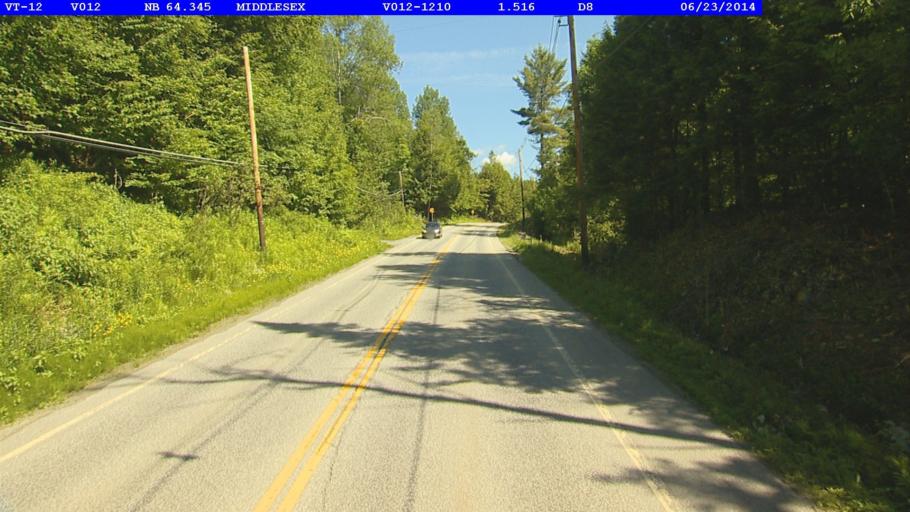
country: US
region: Vermont
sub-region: Washington County
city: Montpelier
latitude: 44.3263
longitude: -72.5799
